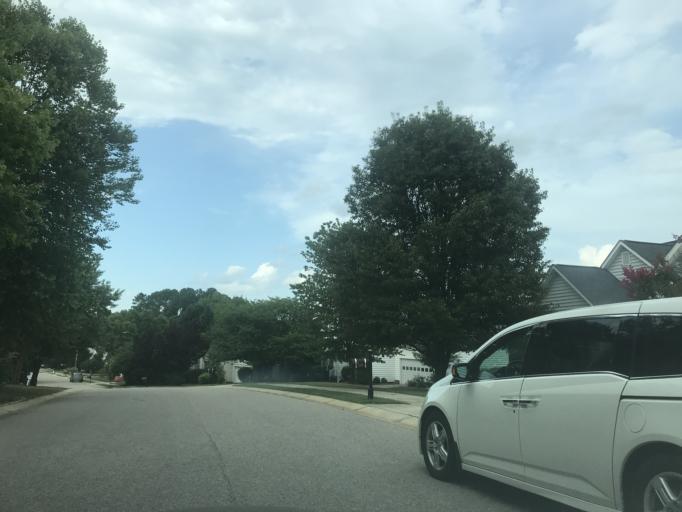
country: US
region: North Carolina
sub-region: Wake County
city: Knightdale
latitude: 35.8363
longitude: -78.5571
